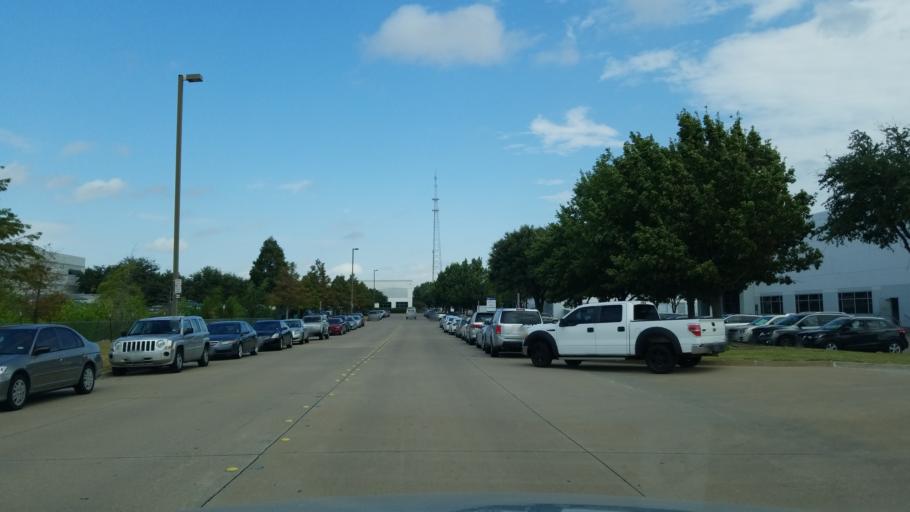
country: US
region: Texas
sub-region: Dallas County
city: Garland
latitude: 32.8924
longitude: -96.6876
